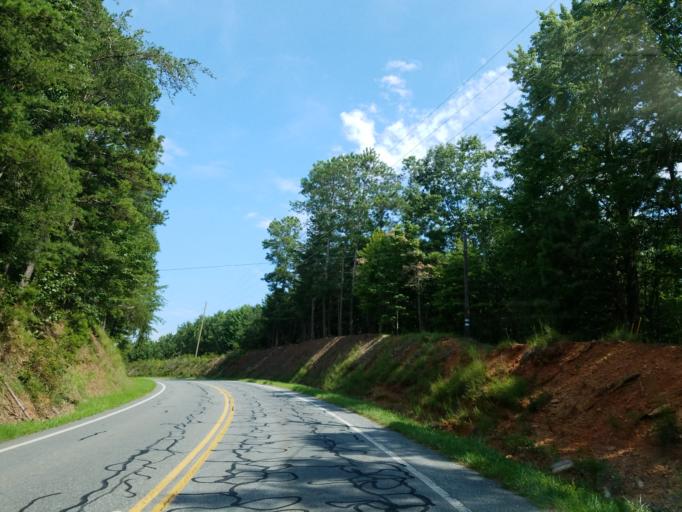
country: US
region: Georgia
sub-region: Gilmer County
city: Ellijay
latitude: 34.5826
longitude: -84.6095
